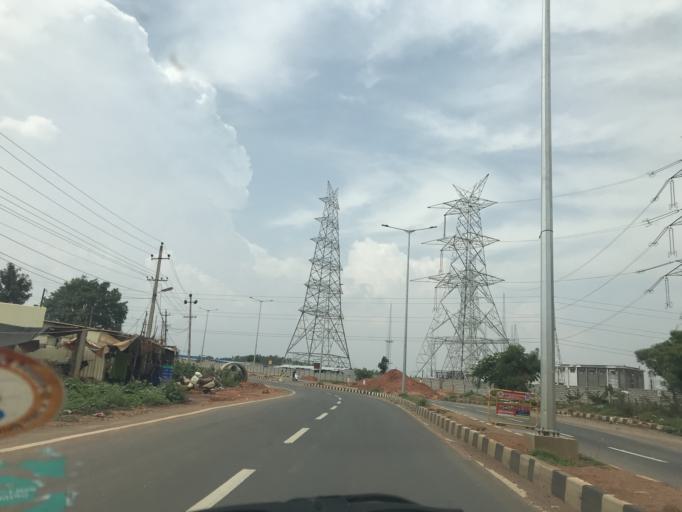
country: IN
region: Karnataka
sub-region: Bangalore Urban
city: Yelahanka
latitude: 13.1435
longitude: 77.6728
